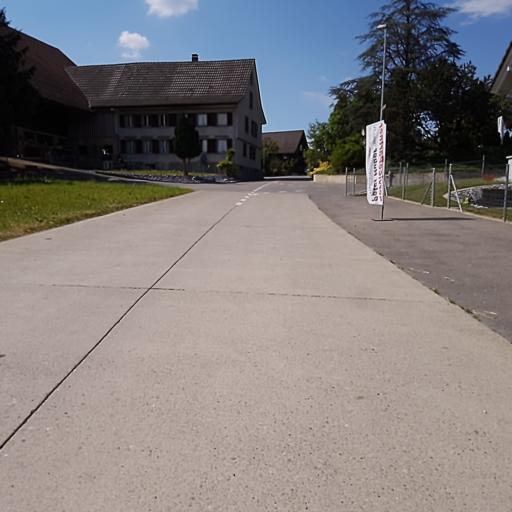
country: CH
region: Thurgau
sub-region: Arbon District
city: Amriswil
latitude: 47.5616
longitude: 9.3001
